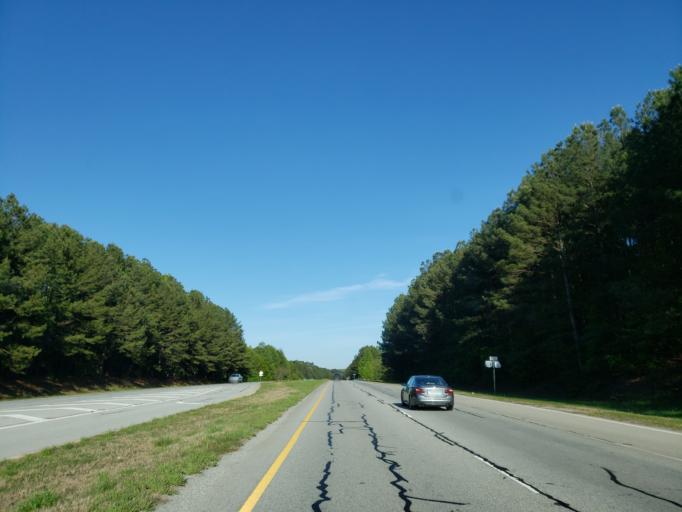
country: US
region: Georgia
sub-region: Paulding County
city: Dallas
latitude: 33.9146
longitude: -84.9177
